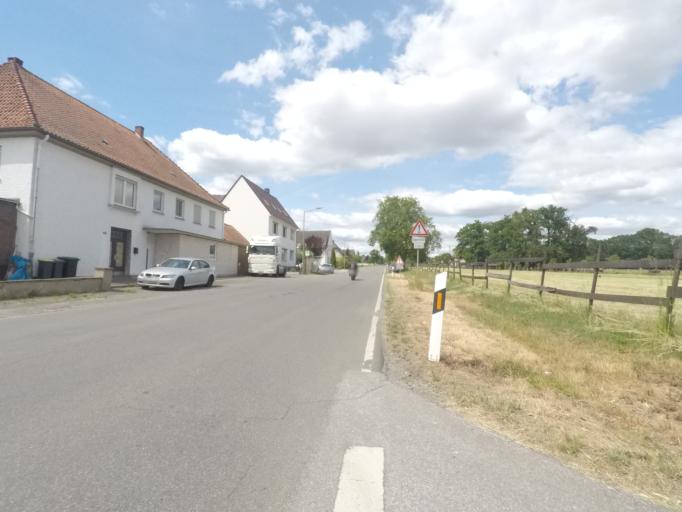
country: DE
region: North Rhine-Westphalia
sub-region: Regierungsbezirk Detmold
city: Rodinghausen
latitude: 52.2098
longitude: 8.5119
